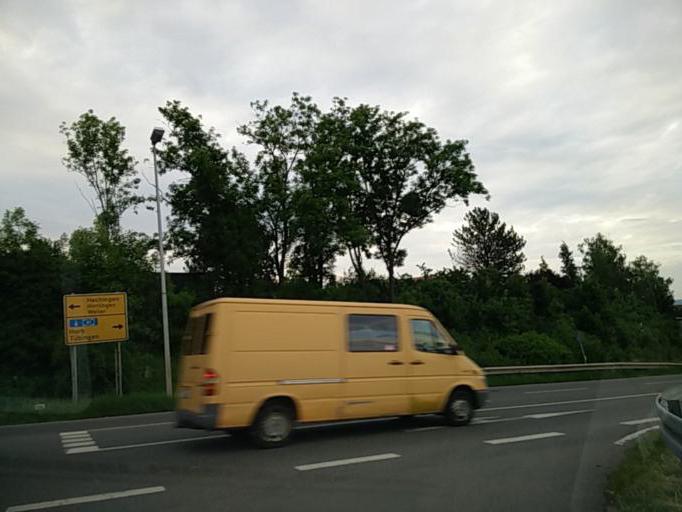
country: DE
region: Baden-Wuerttemberg
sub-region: Tuebingen Region
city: Rottenburg
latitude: 48.4650
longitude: 8.9361
